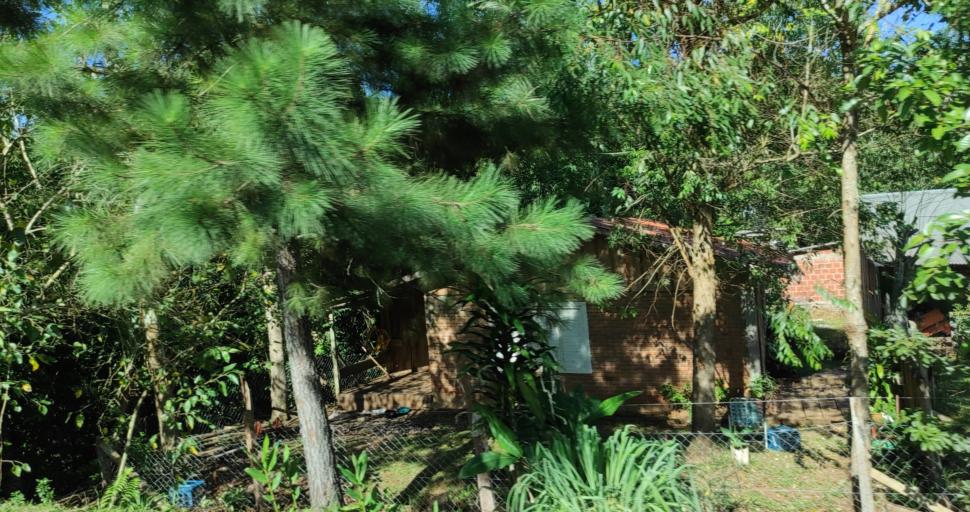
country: AR
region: Misiones
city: El Soberbio
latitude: -27.2428
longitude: -54.0389
